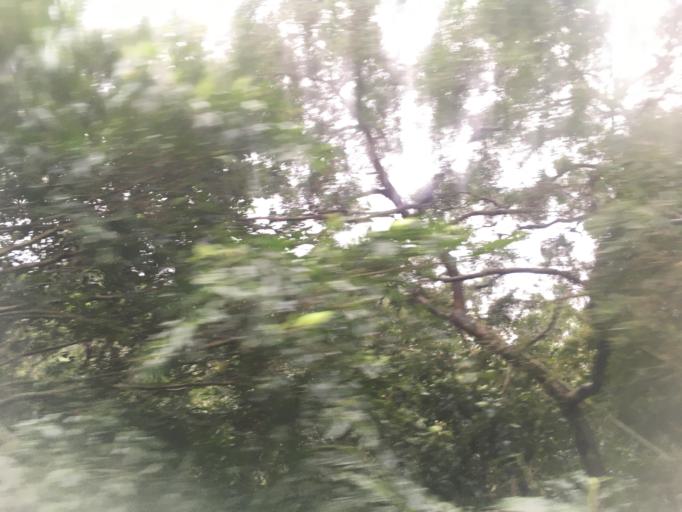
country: TW
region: Taiwan
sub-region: Keelung
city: Keelung
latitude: 25.0694
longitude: 121.9057
